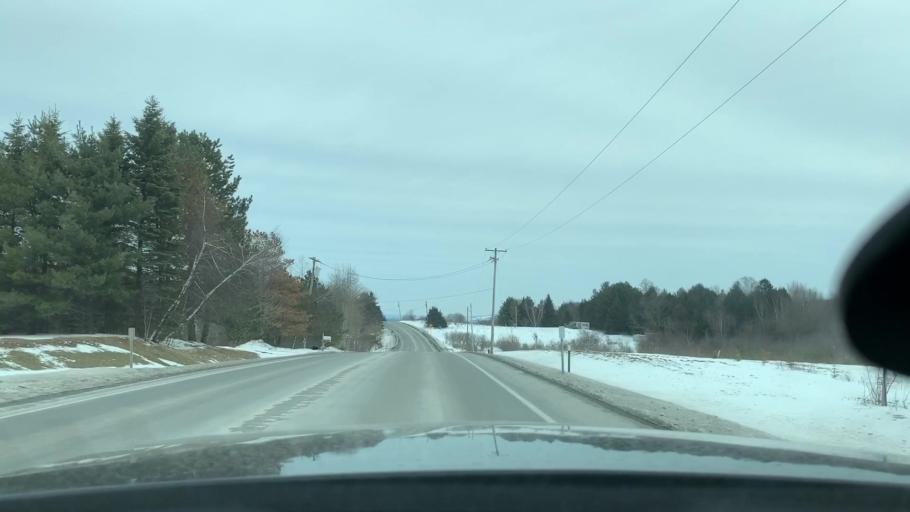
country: US
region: New York
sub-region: Herkimer County
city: Frankfort
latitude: 43.0305
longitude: -75.1664
